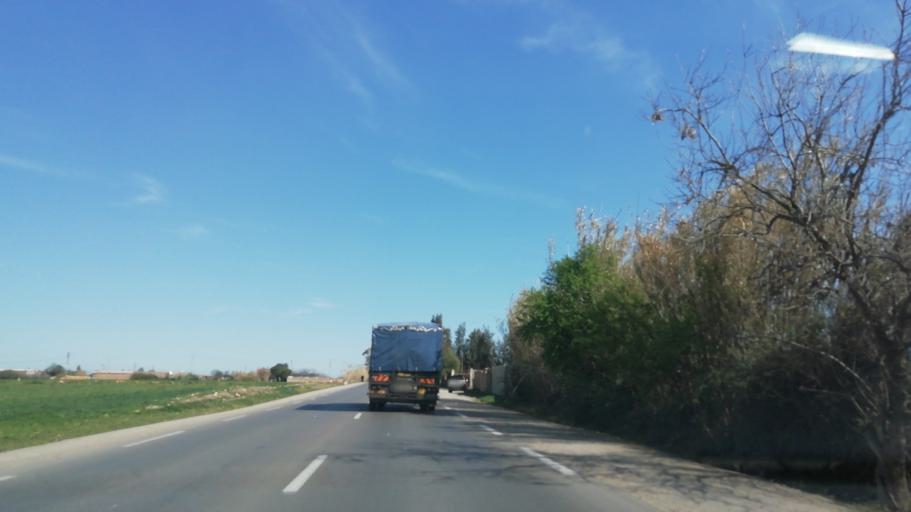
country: DZ
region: Mascara
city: Mascara
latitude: 35.4146
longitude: 0.3839
